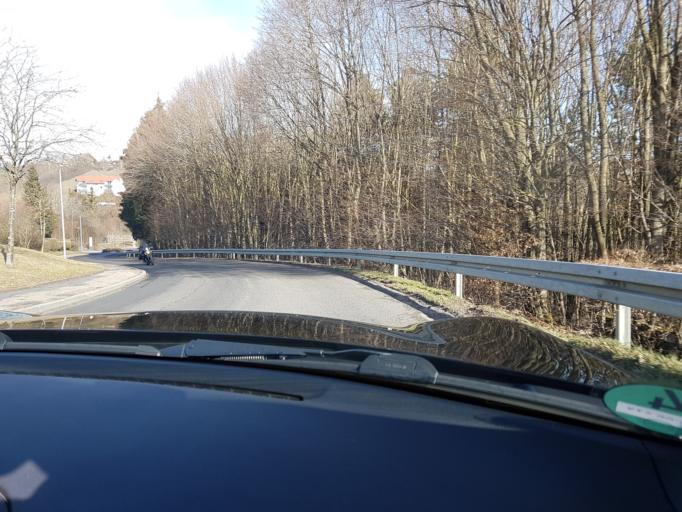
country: DE
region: Baden-Wuerttemberg
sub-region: Regierungsbezirk Stuttgart
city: Krautheim
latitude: 49.3896
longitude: 9.6327
